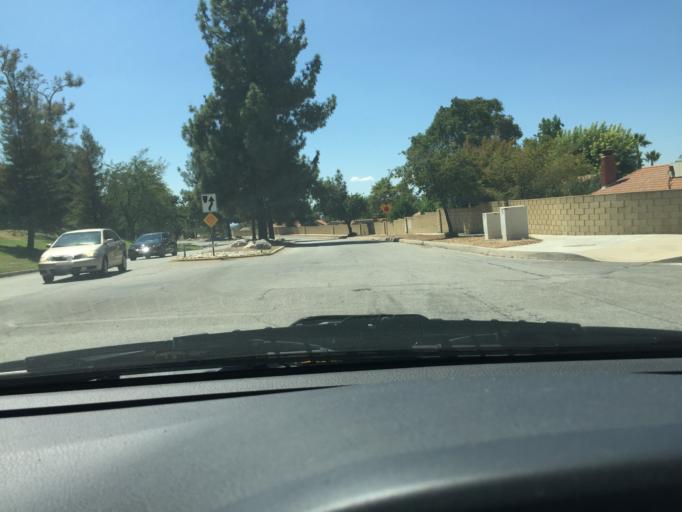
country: US
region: California
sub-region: San Bernardino County
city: Yucaipa
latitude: 34.0058
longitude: -117.0177
